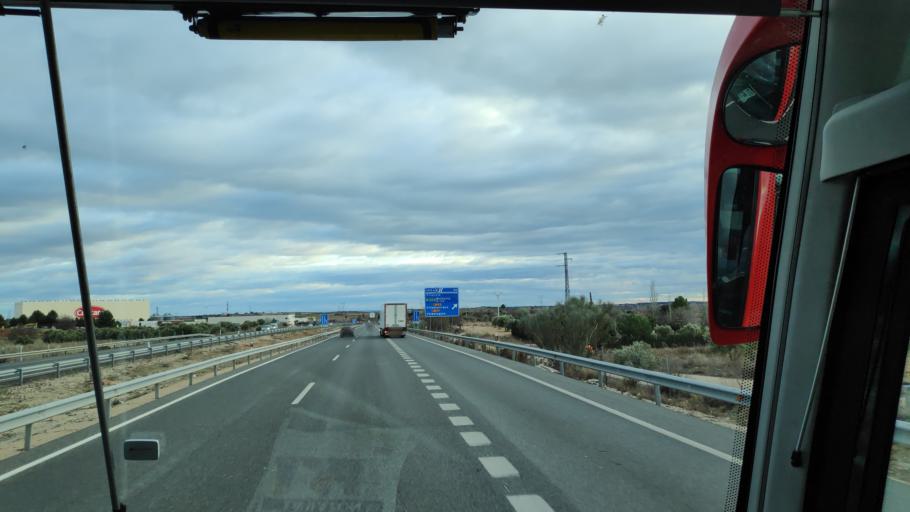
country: ES
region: Madrid
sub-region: Provincia de Madrid
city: Villarejo de Salvanes
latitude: 40.1815
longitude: -3.2971
